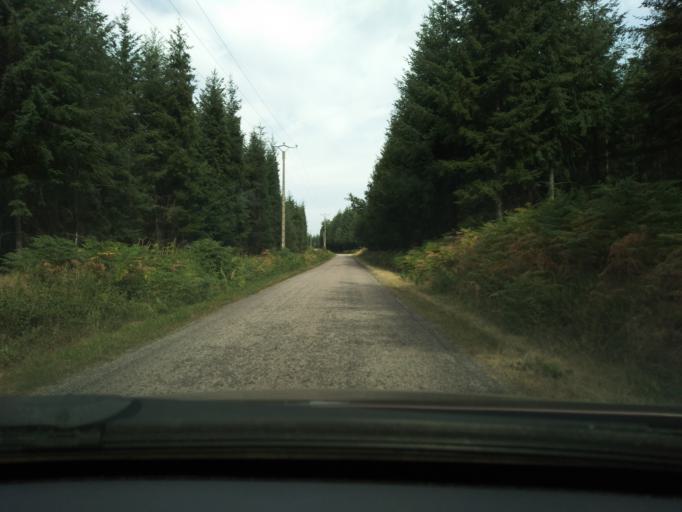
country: FR
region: Bourgogne
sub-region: Departement de la Cote-d'Or
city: Saulieu
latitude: 47.3692
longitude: 4.0865
